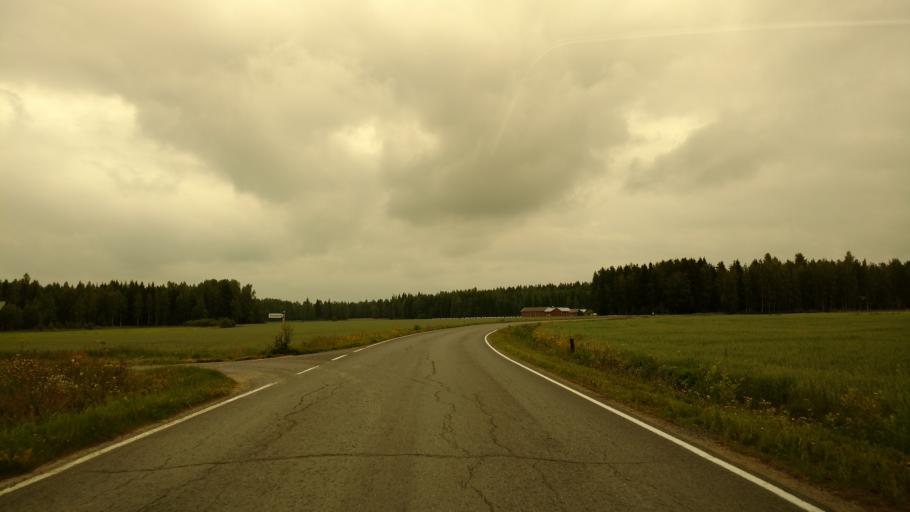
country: FI
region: Varsinais-Suomi
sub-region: Loimaa
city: Koski Tl
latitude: 60.7365
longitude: 23.1917
